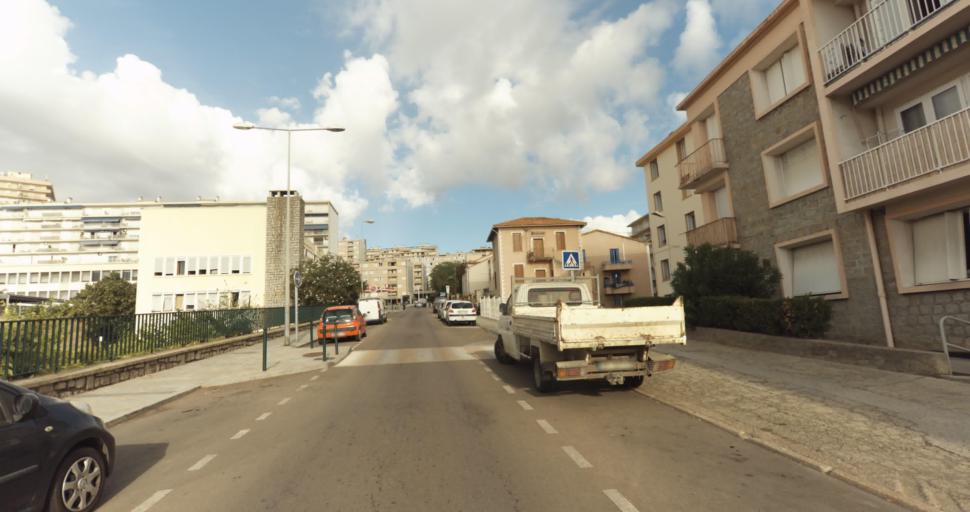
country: FR
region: Corsica
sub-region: Departement de la Corse-du-Sud
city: Ajaccio
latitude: 41.9307
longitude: 8.7368
